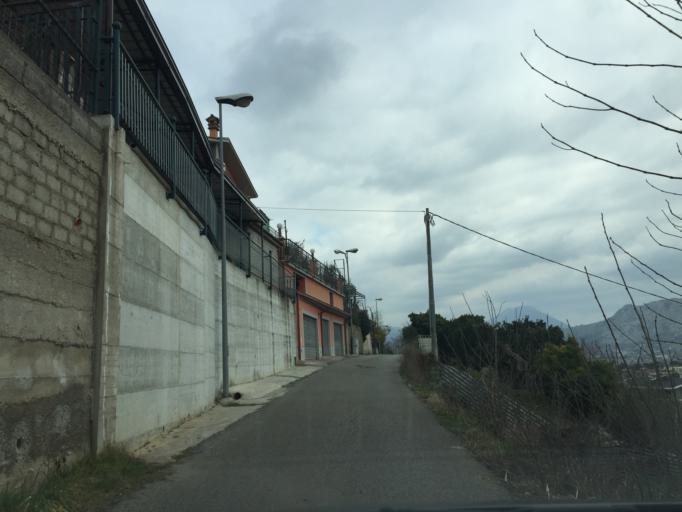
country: IT
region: Latium
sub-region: Provincia di Frosinone
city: Cassino
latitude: 41.4812
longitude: 13.8129
